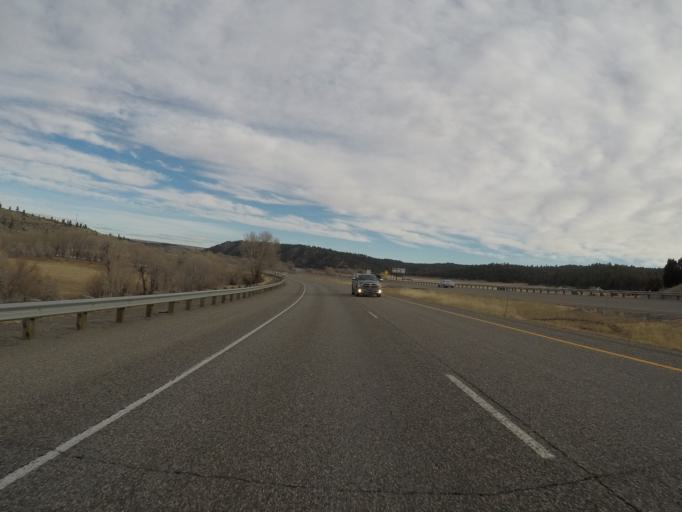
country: US
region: Montana
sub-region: Stillwater County
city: Absarokee
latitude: 45.6814
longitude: -109.4364
